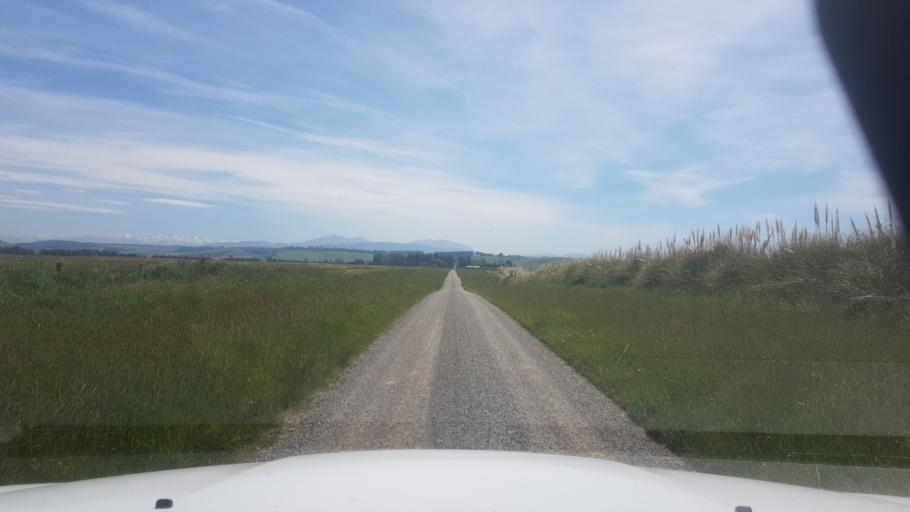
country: NZ
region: Canterbury
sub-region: Timaru District
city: Pleasant Point
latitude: -44.2331
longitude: 171.1674
